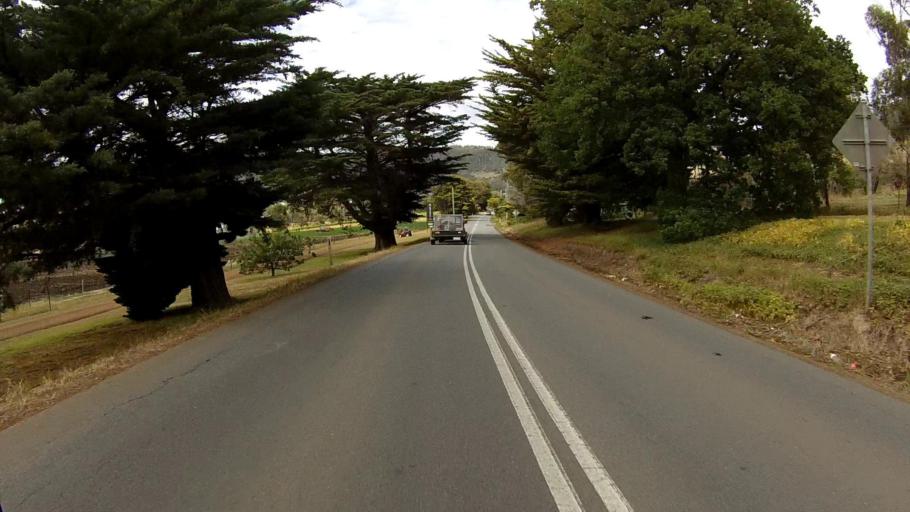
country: AU
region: Tasmania
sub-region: Clarence
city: Cambridge
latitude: -42.8265
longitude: 147.4485
